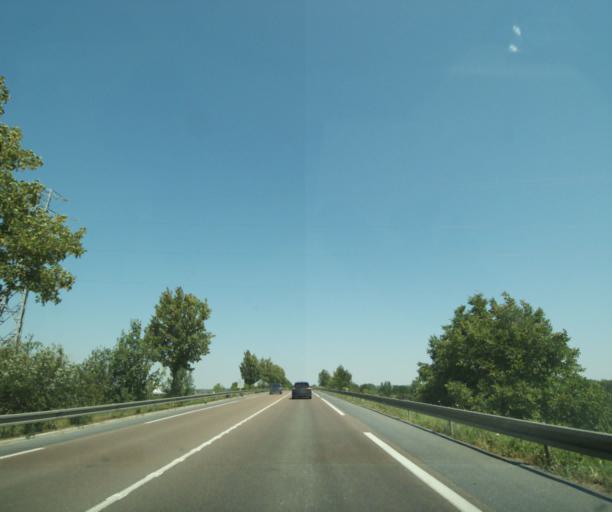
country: FR
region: Champagne-Ardenne
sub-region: Departement de la Marne
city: Frignicourt
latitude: 48.7207
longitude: 4.6303
